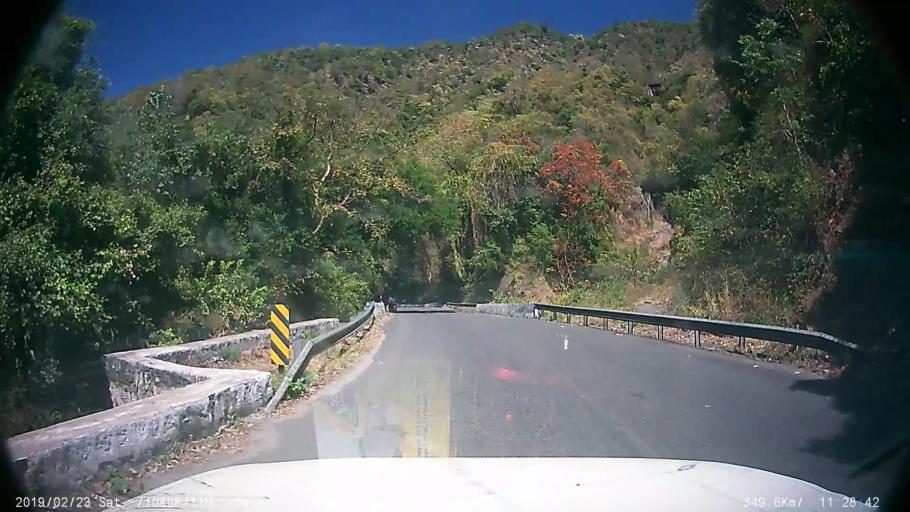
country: IN
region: Tamil Nadu
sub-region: Nilgiri
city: Kotagiri
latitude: 11.3404
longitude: 76.8637
